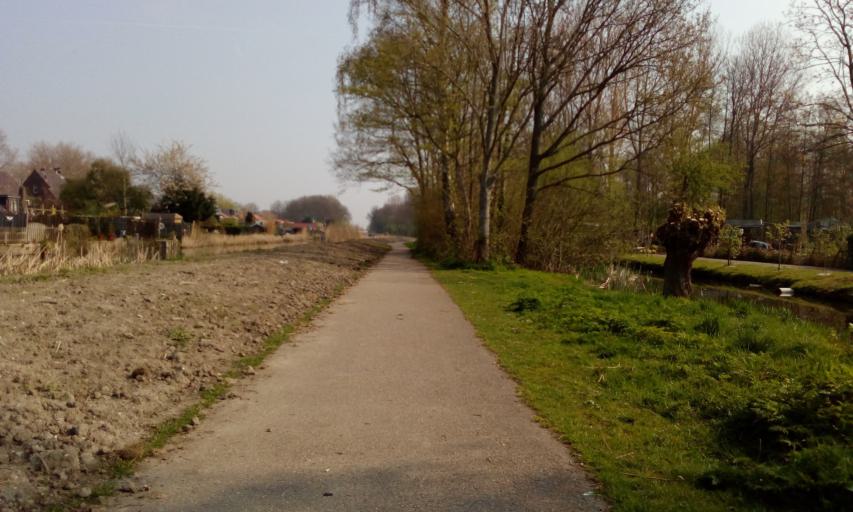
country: NL
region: South Holland
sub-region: Gemeente Capelle aan den IJssel
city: Capelle aan den IJssel
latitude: 51.9294
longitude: 4.5665
